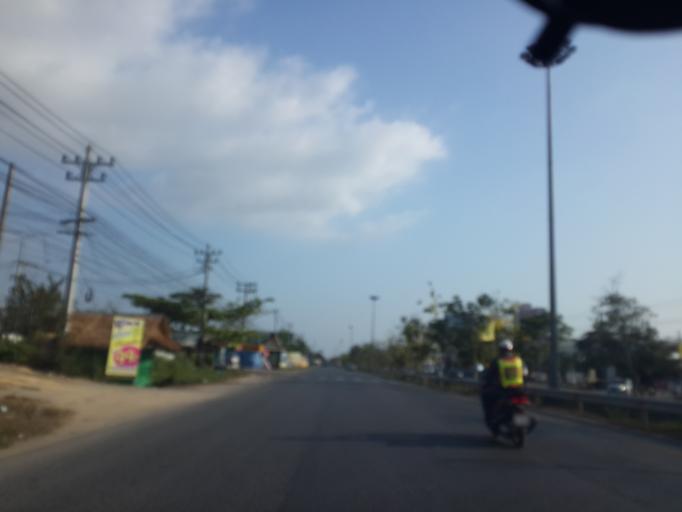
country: TH
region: Chon Buri
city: Phatthaya
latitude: 12.8498
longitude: 100.9090
